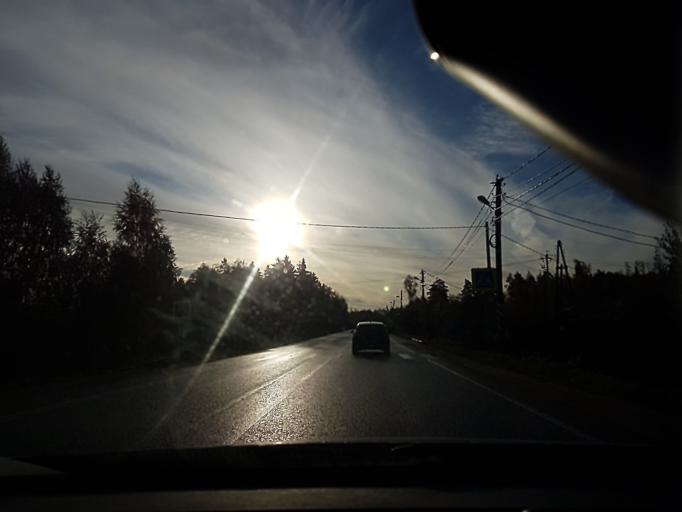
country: RU
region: Moskovskaya
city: Rozhdestveno
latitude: 55.8366
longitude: 37.0139
